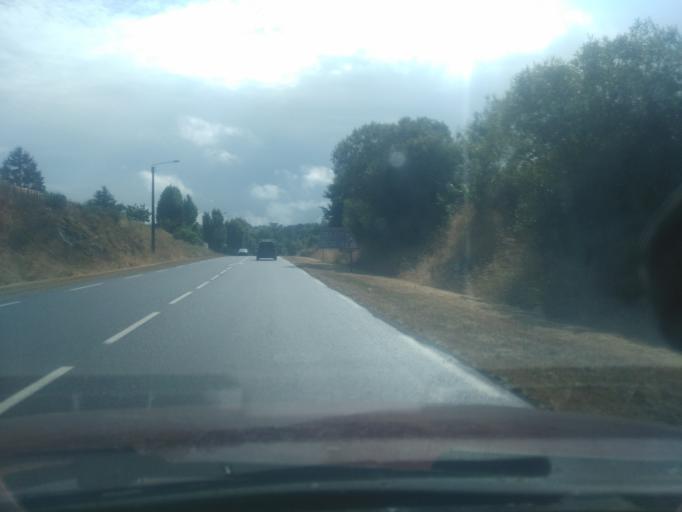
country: FR
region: Poitou-Charentes
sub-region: Departement des Deux-Sevres
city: Parthenay
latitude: 46.6388
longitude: -0.2686
